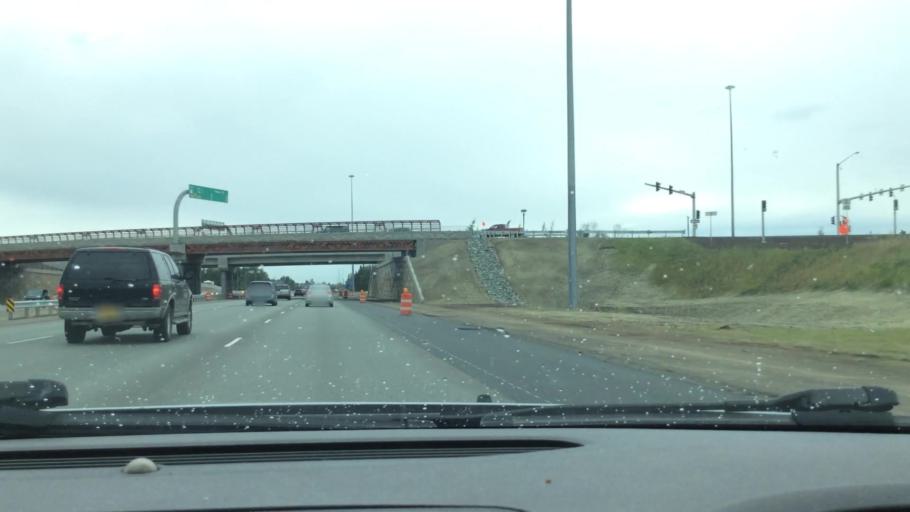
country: US
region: Alaska
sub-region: Anchorage Municipality
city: Elmendorf Air Force Base
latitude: 61.2279
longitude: -149.7307
